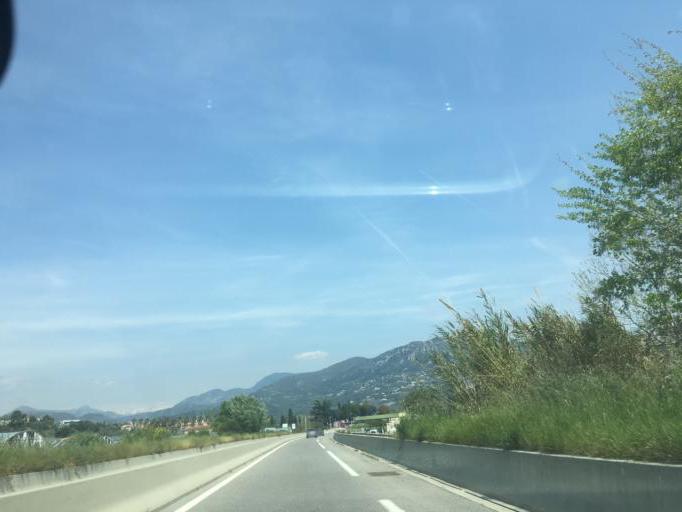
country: FR
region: Provence-Alpes-Cote d'Azur
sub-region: Departement des Alpes-Maritimes
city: Gattieres
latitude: 43.7630
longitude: 7.1980
